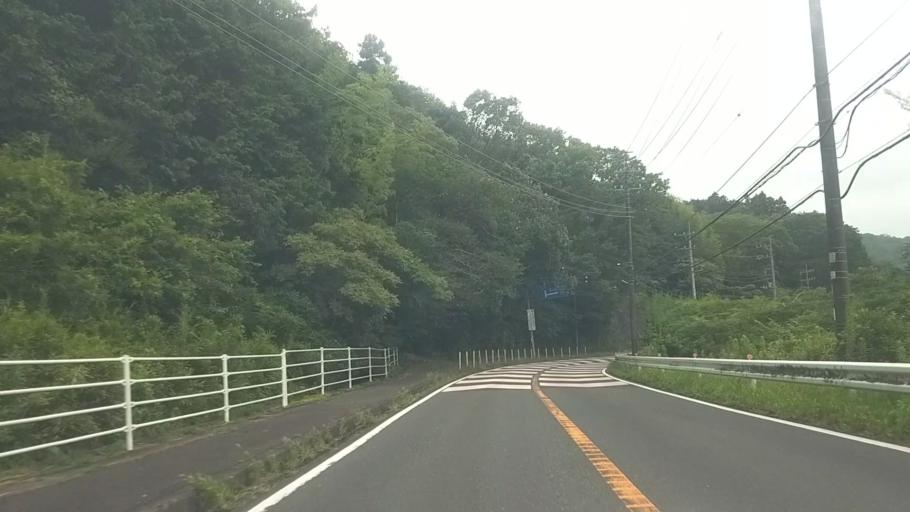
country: JP
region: Chiba
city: Kawaguchi
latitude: 35.2615
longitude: 140.0609
